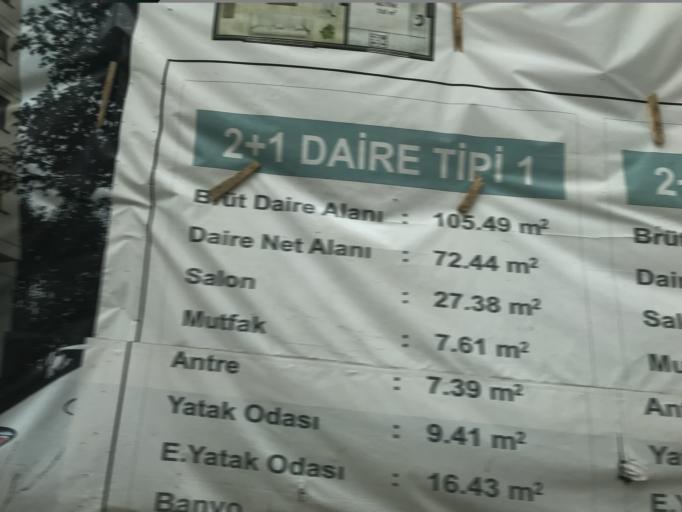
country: TR
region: Istanbul
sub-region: Atasehir
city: Atasehir
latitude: 40.9621
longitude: 29.0969
